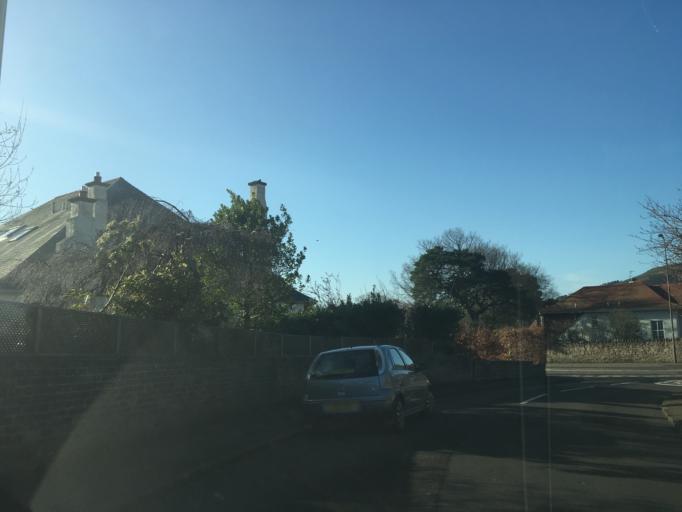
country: GB
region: Scotland
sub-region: Midlothian
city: Loanhead
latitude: 55.9001
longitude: -3.1984
